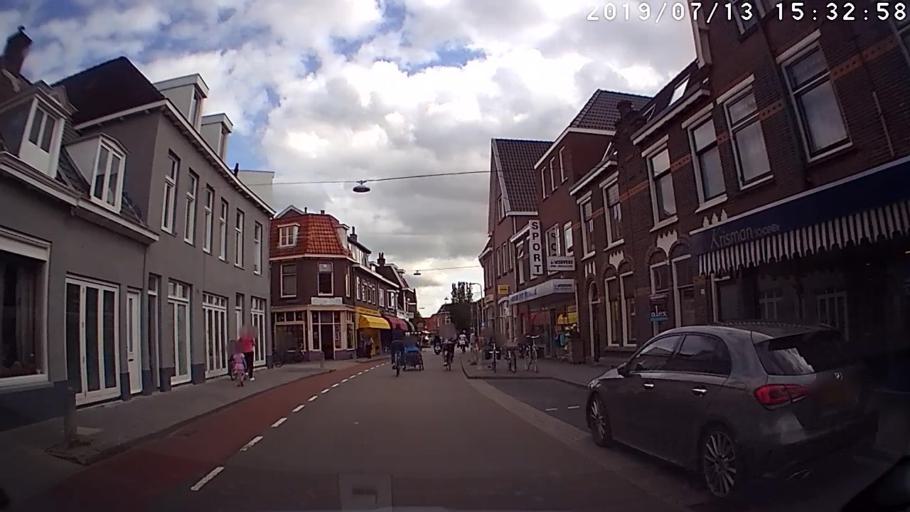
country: NL
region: Overijssel
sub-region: Gemeente Zwolle
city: Zwolle
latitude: 52.5060
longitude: 6.1019
